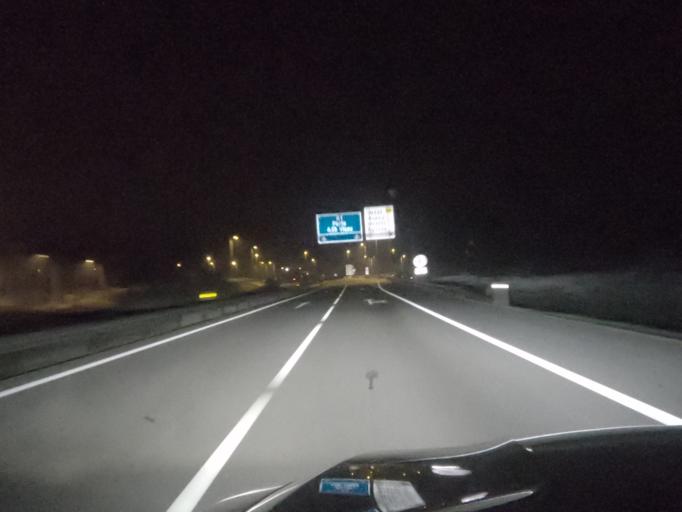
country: PT
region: Aveiro
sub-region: Oliveira do Bairro
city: Oia
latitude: 40.5667
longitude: -8.5606
